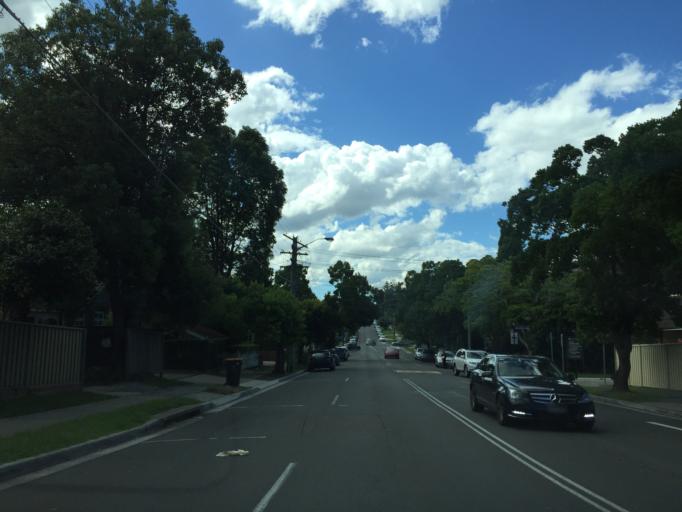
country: AU
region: New South Wales
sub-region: Ryde
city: West Ryde
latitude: -33.7923
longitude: 151.0772
